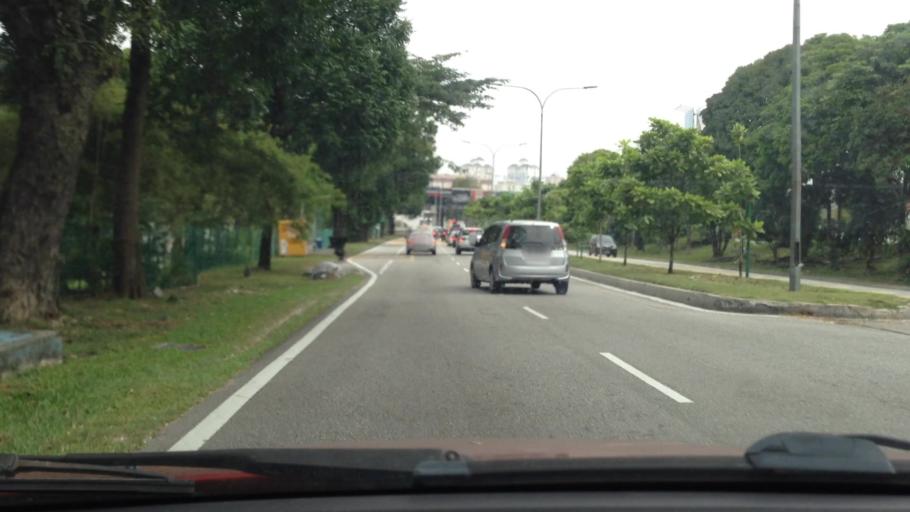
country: MY
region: Selangor
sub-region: Petaling
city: Petaling Jaya
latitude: 3.0934
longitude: 101.6073
